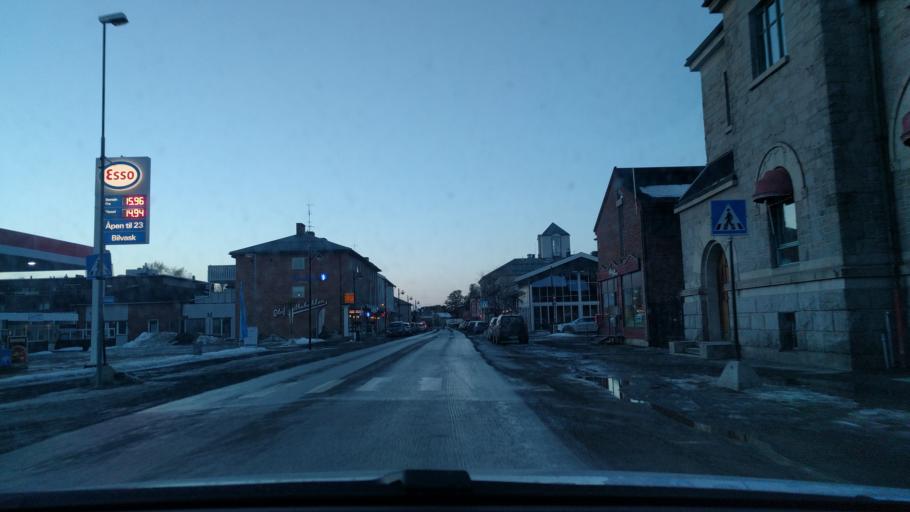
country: NO
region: Hedmark
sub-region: Elverum
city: Elverum
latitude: 60.8799
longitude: 11.5642
